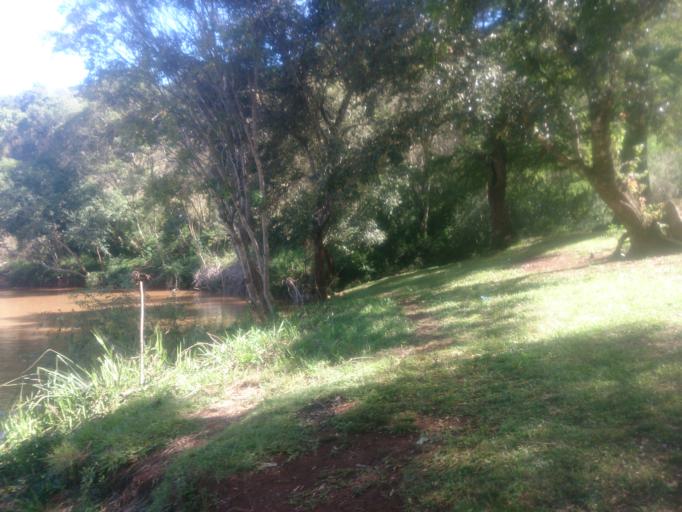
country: AR
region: Misiones
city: Campo Viera
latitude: -27.3826
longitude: -55.0153
